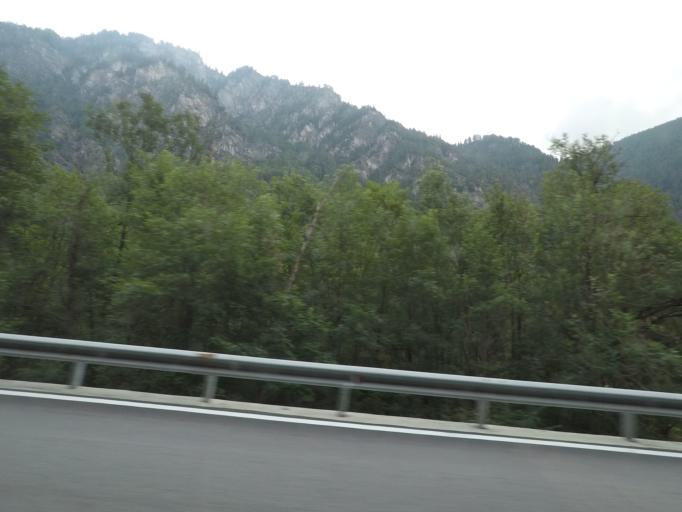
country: IT
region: Aosta Valley
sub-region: Valle d'Aosta
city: Chamois
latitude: 45.8390
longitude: 7.6040
